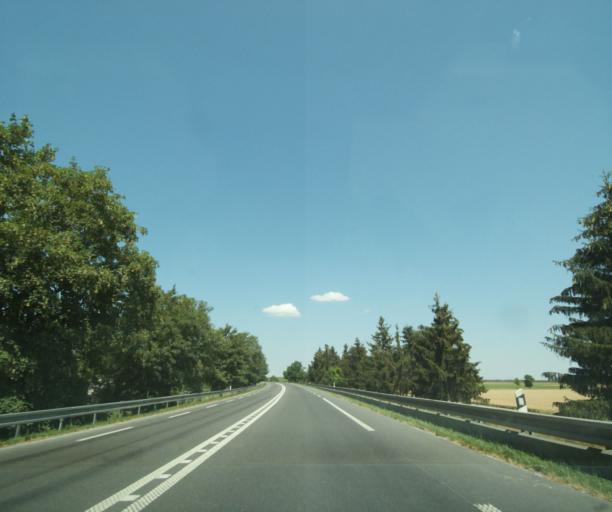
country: FR
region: Champagne-Ardenne
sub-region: Departement de la Marne
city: Verzy
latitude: 49.1376
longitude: 4.2296
